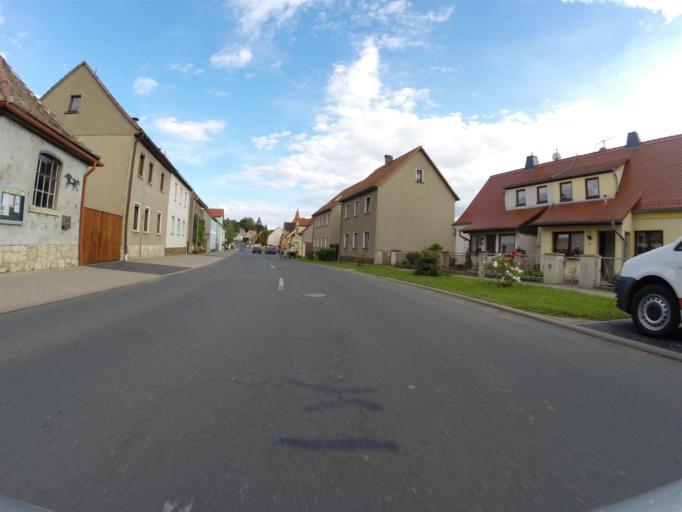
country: DE
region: Thuringia
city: Mellingen
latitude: 50.9448
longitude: 11.3914
